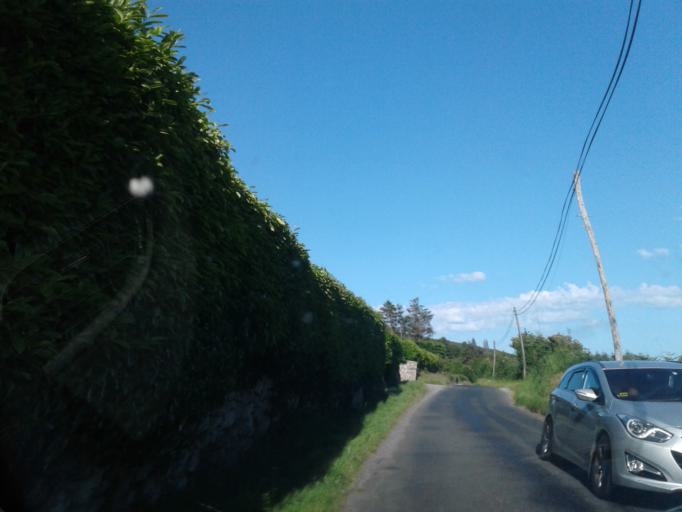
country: IE
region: Leinster
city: Ballinteer
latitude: 53.1901
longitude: -6.2551
